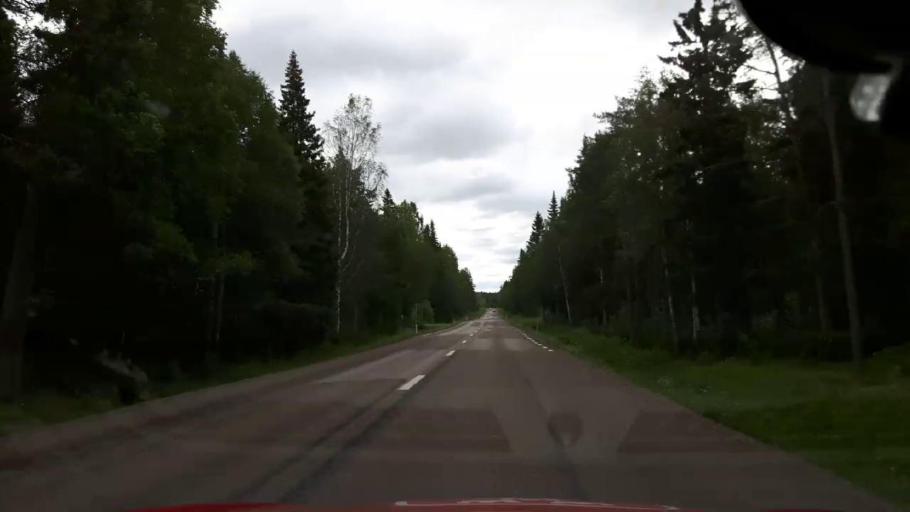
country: SE
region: Jaemtland
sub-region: OEstersunds Kommun
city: Brunflo
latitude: 63.0366
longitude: 14.8900
